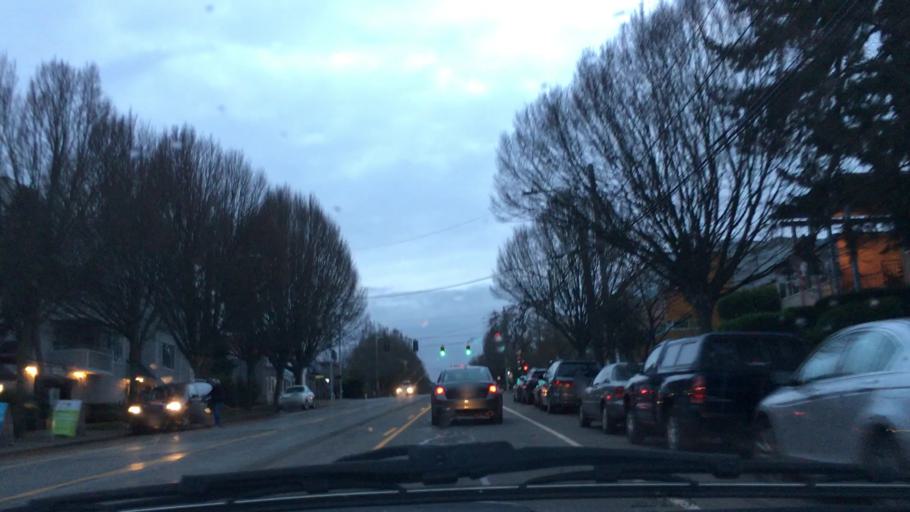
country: US
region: Washington
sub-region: King County
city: White Center
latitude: 47.5219
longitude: -122.3767
